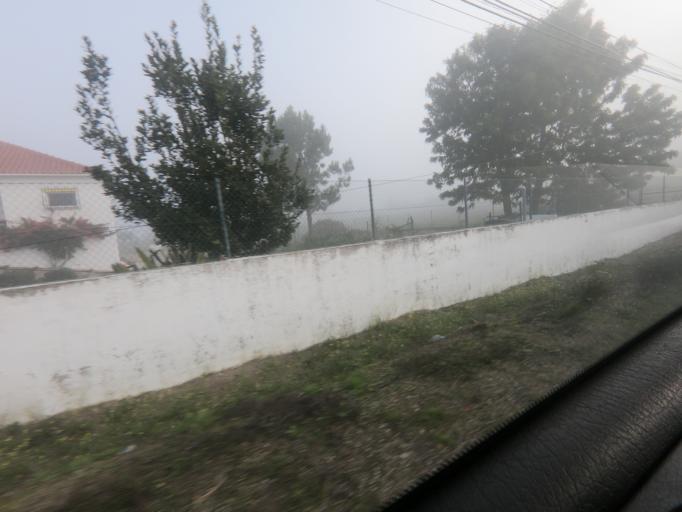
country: PT
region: Setubal
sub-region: Palmela
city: Pinhal Novo
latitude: 38.6114
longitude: -8.8741
